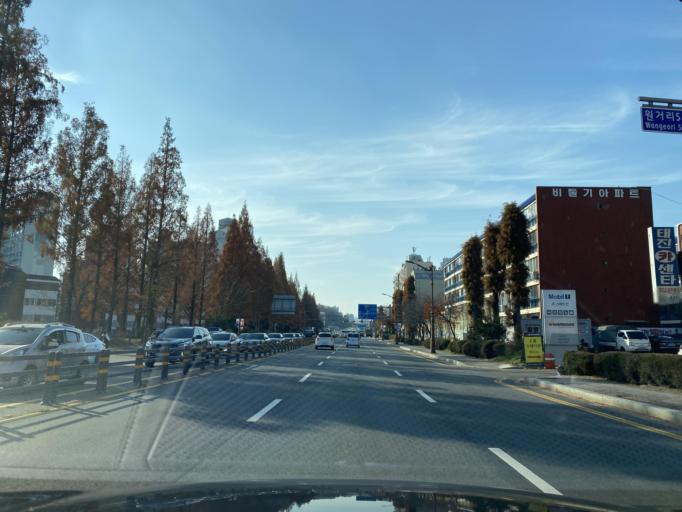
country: KR
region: Chungcheongnam-do
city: Cheonan
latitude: 36.7987
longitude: 127.1580
